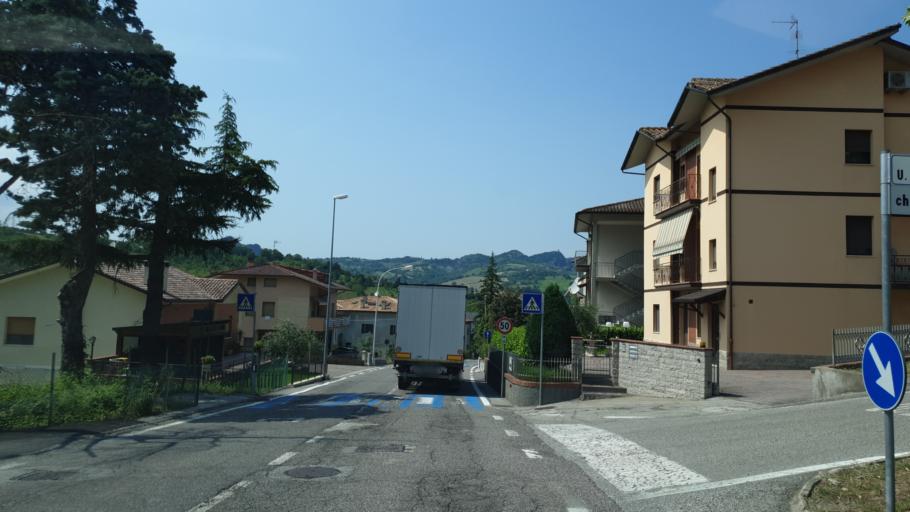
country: SM
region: Acquaviva
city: Acquaviva
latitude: 43.9496
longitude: 12.4075
